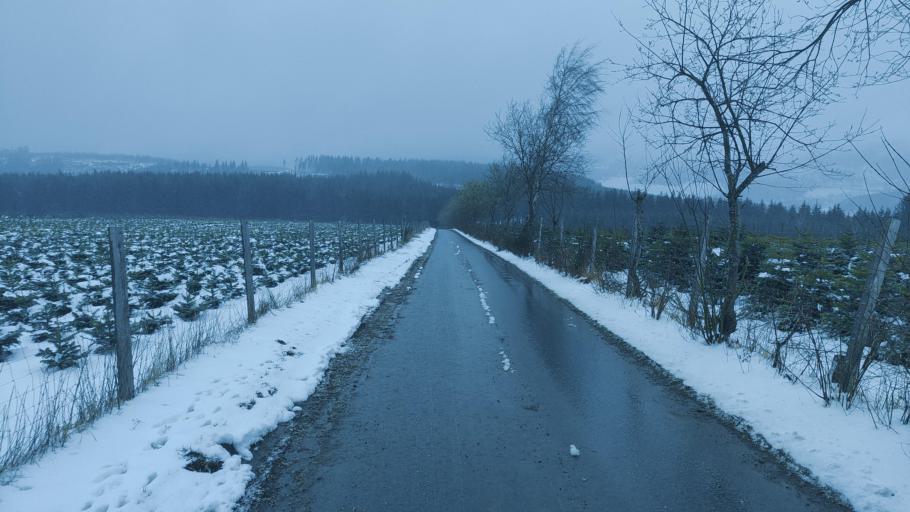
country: DE
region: North Rhine-Westphalia
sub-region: Regierungsbezirk Arnsberg
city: Bad Berleburg
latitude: 51.1500
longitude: 8.4195
